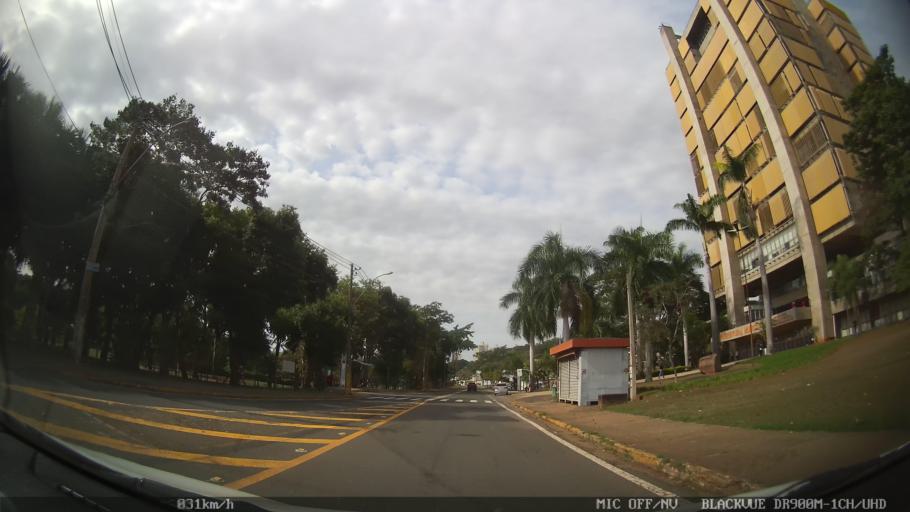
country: BR
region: Sao Paulo
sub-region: Piracicaba
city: Piracicaba
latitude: -22.7283
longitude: -47.6646
